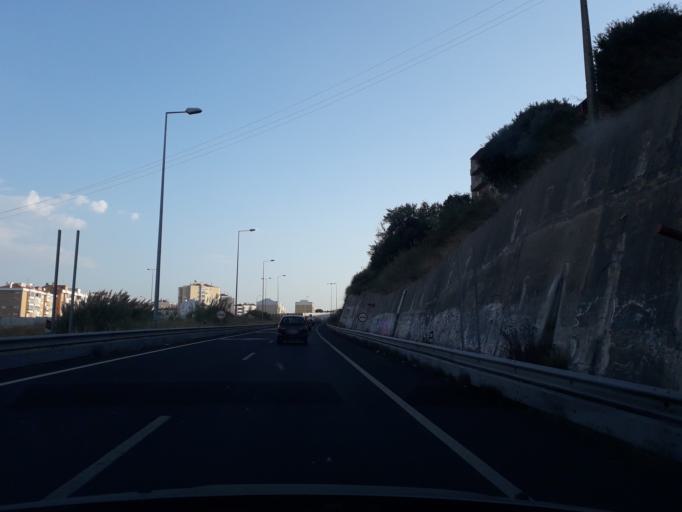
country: PT
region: Lisbon
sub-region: Odivelas
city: Pontinha
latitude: 38.7682
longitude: -9.2107
